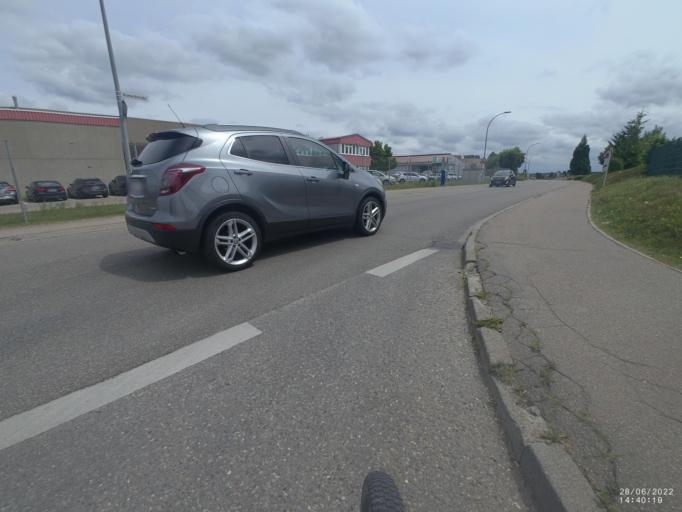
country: DE
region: Baden-Wuerttemberg
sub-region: Regierungsbezirk Stuttgart
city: Gerstetten
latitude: 48.6281
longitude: 10.0107
